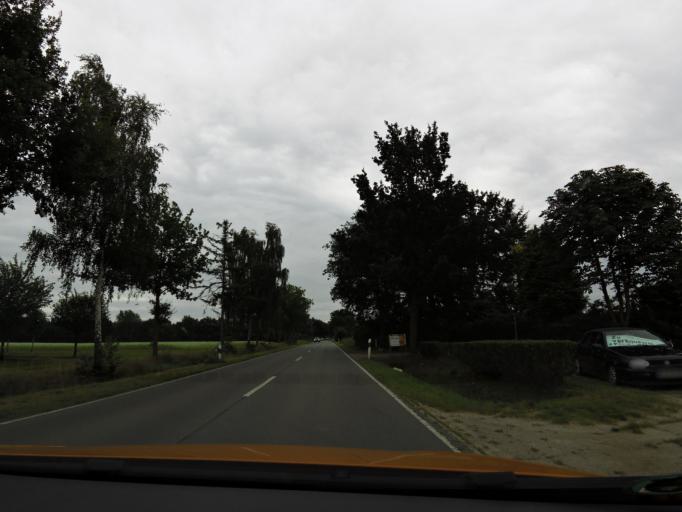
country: DE
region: Lower Saxony
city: Westerstede
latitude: 53.2491
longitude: 7.9738
